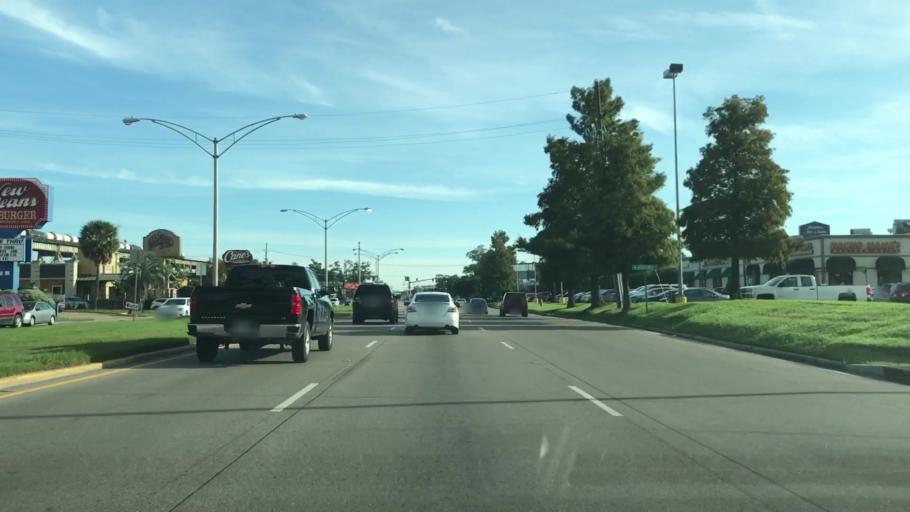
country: US
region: Louisiana
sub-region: Jefferson Parish
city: Elmwood
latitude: 29.9600
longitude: -90.1838
